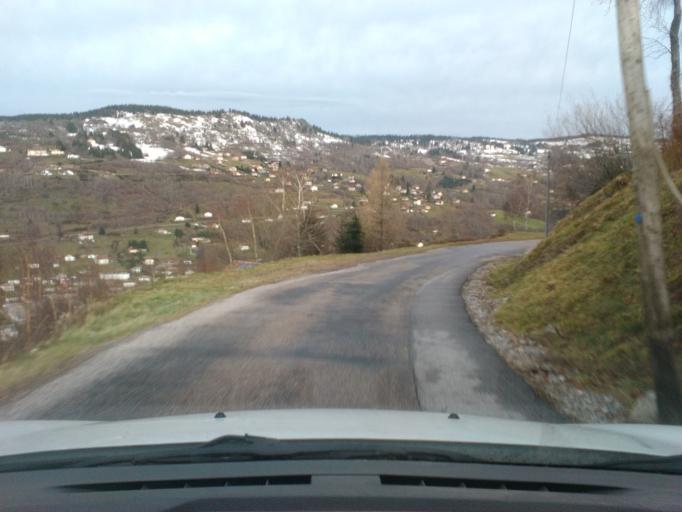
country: FR
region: Lorraine
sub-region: Departement des Vosges
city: La Bresse
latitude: 48.0012
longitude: 6.8817
